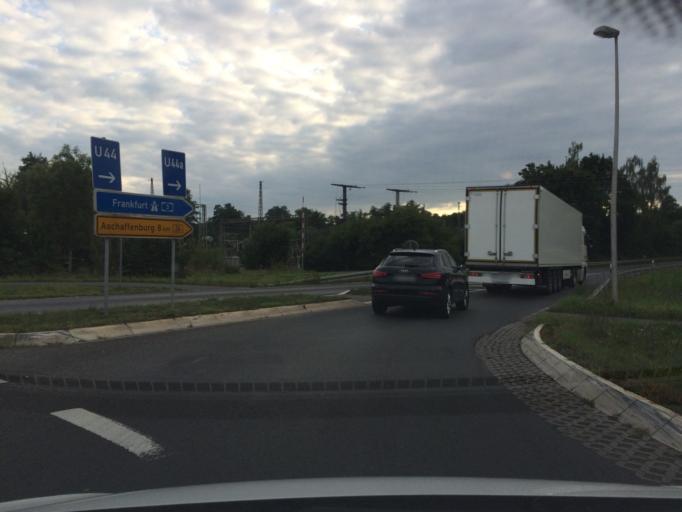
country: DE
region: Bavaria
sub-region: Regierungsbezirk Unterfranken
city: Sailauf
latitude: 50.0070
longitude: 9.2422
